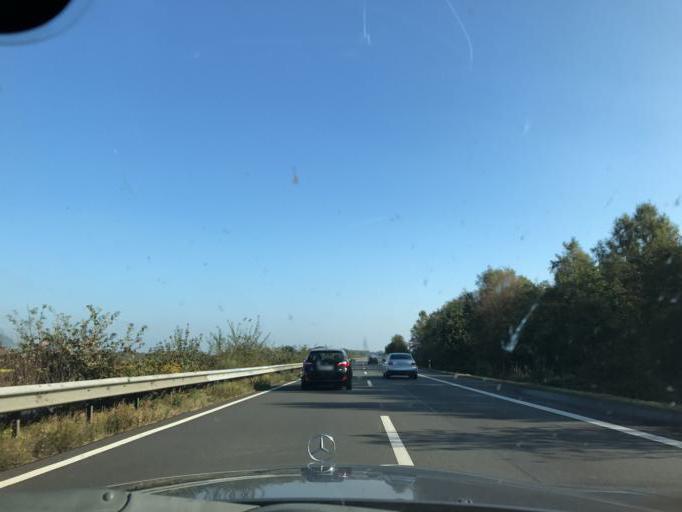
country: DE
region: Lower Saxony
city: Westerstede
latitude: 53.2880
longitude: 7.8666
